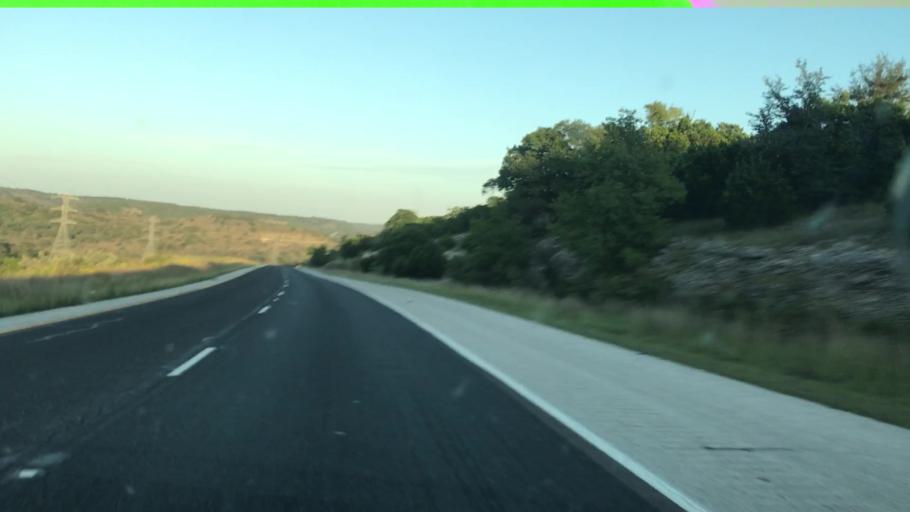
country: US
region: Texas
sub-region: Kerr County
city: Kerrville
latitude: 30.0525
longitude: -99.0208
